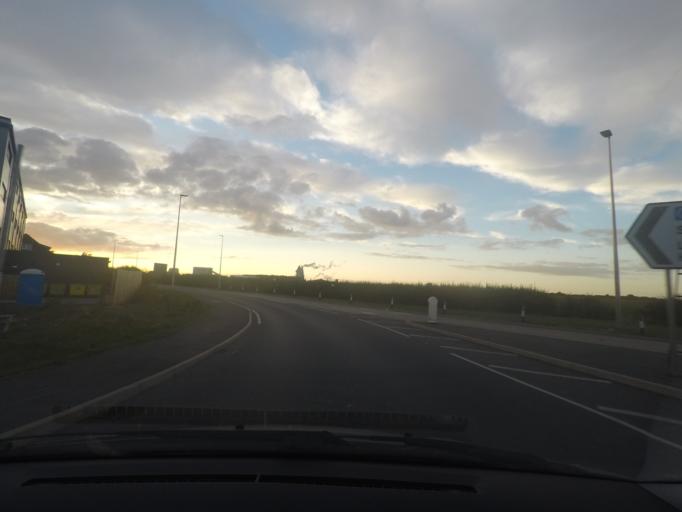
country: GB
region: England
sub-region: North Lincolnshire
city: Croxton
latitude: 53.5846
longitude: -0.3517
